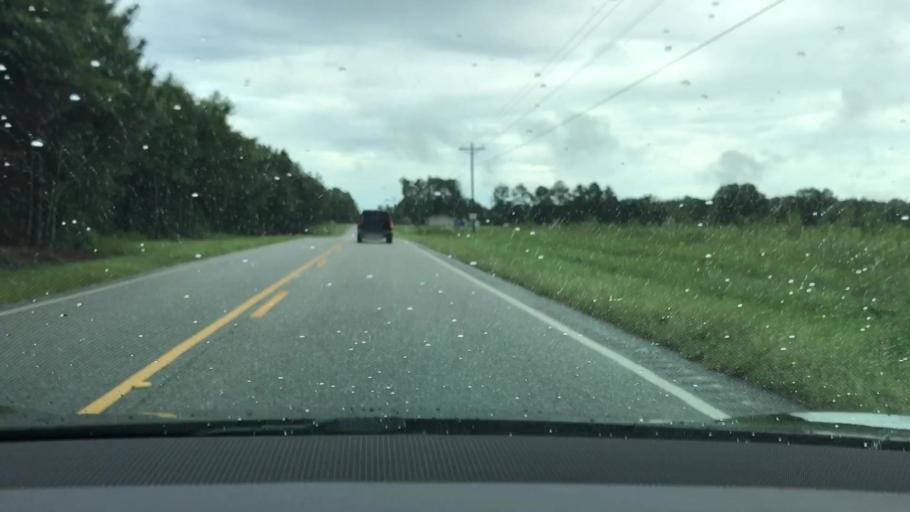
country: US
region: Alabama
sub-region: Geneva County
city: Samson
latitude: 31.0944
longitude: -86.1111
